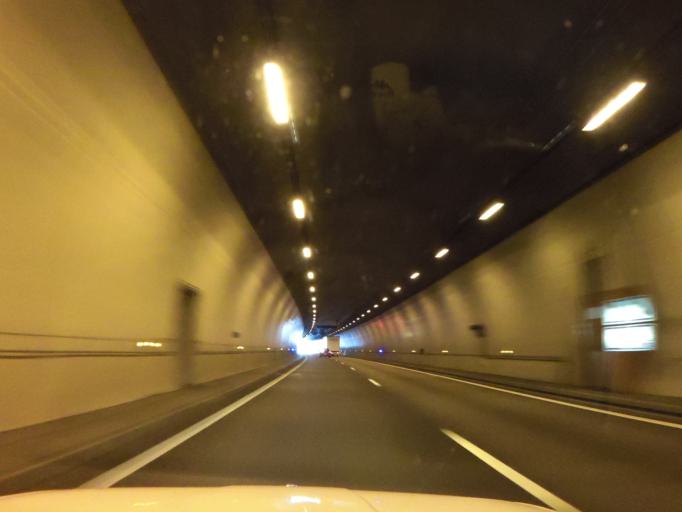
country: FR
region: Rhone-Alpes
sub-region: Departement de la Savoie
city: Aiton
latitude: 45.5363
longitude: 6.3081
